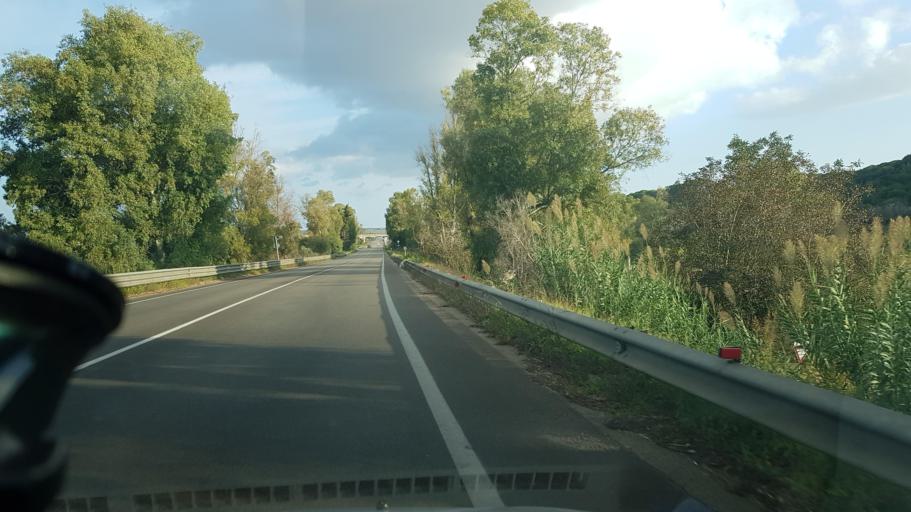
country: IT
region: Apulia
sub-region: Provincia di Lecce
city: Acquarica del Capo
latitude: 39.9042
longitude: 18.2448
